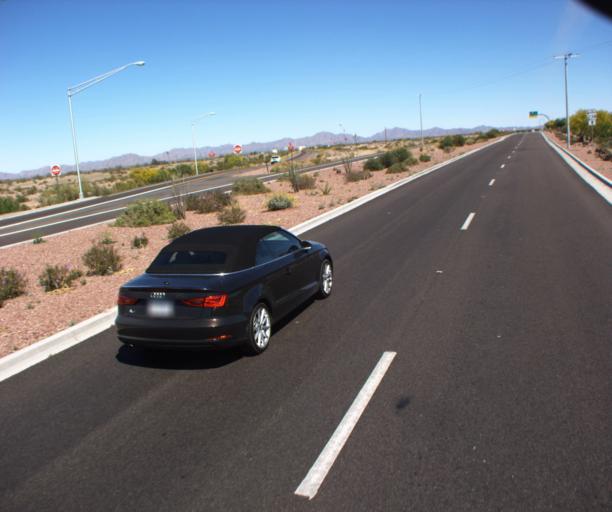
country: US
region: Arizona
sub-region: Maricopa County
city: Gila Bend
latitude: 32.9529
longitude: -112.6914
